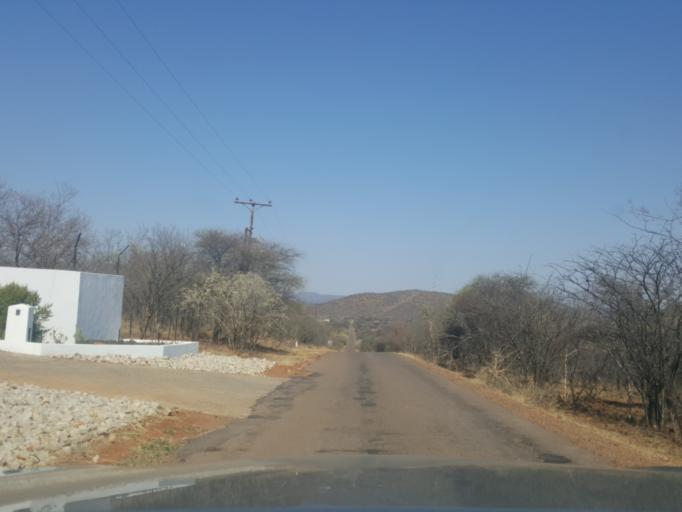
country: BW
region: Kweneng
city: Gabane
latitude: -24.7407
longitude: 25.8187
